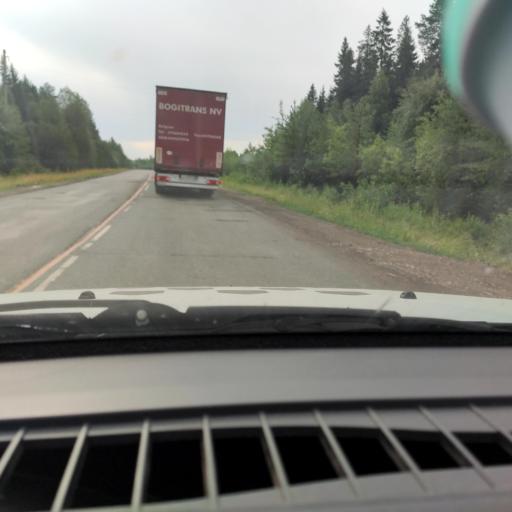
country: RU
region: Kirov
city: Kostino
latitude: 58.8192
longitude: 53.3166
